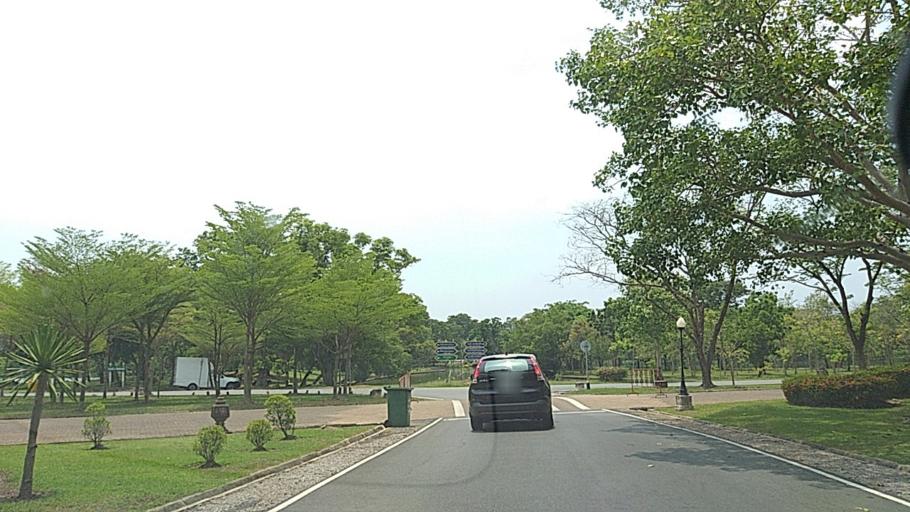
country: TH
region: Bangkok
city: Thawi Watthana
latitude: 13.7734
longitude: 100.3216
